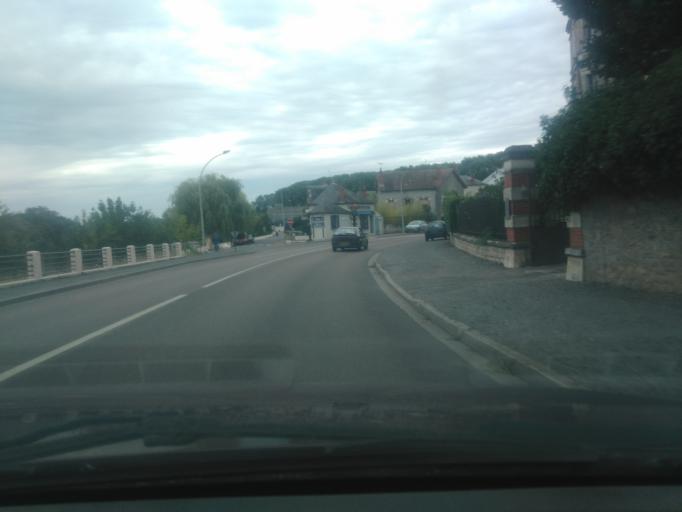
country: FR
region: Bourgogne
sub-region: Departement de la Nievre
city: Decize
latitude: 46.8287
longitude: 3.4587
